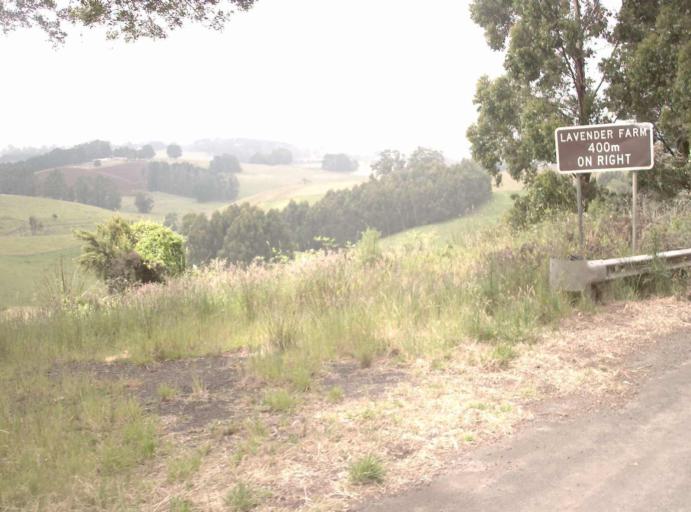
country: AU
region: Victoria
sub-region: Latrobe
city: Moe
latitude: -38.3893
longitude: 146.1233
